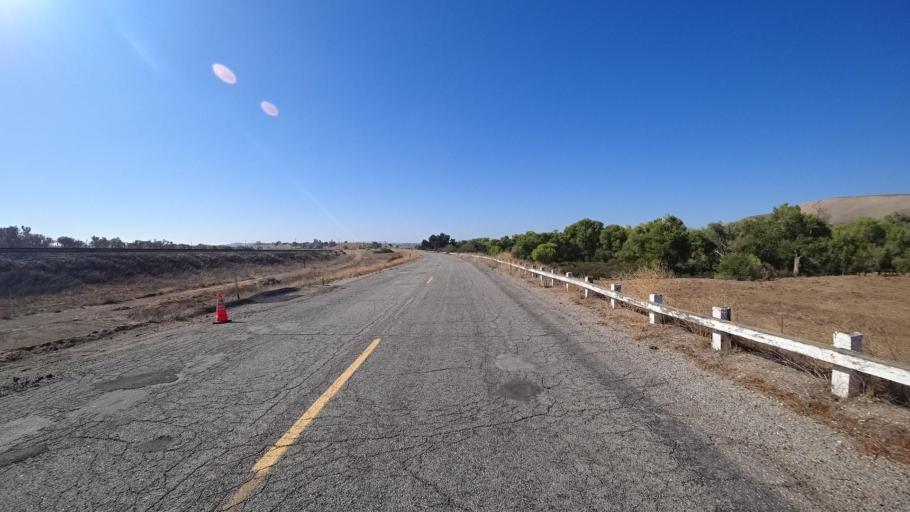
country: US
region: California
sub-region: San Luis Obispo County
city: San Miguel
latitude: 35.8226
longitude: -120.7532
